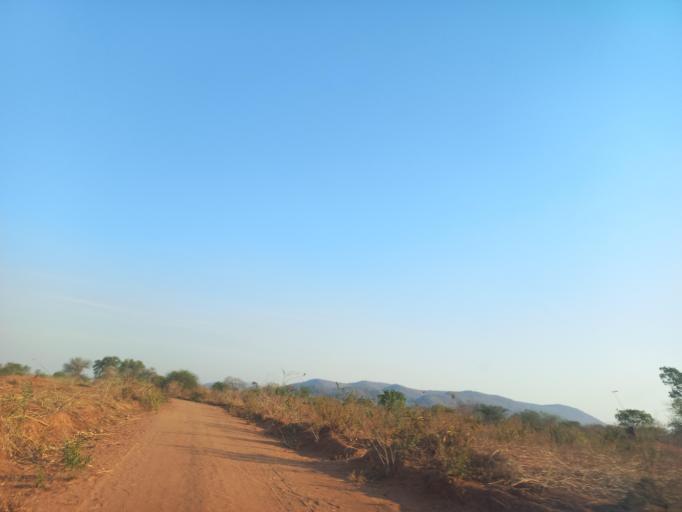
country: ZM
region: Lusaka
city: Luangwa
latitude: -15.4419
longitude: 30.3611
